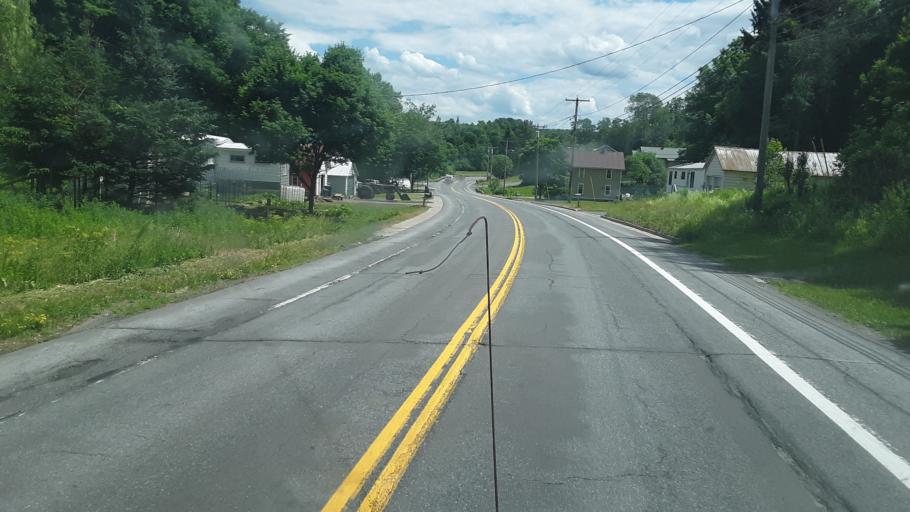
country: US
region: New York
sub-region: Oneida County
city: Rome
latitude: 43.3734
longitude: -75.4837
